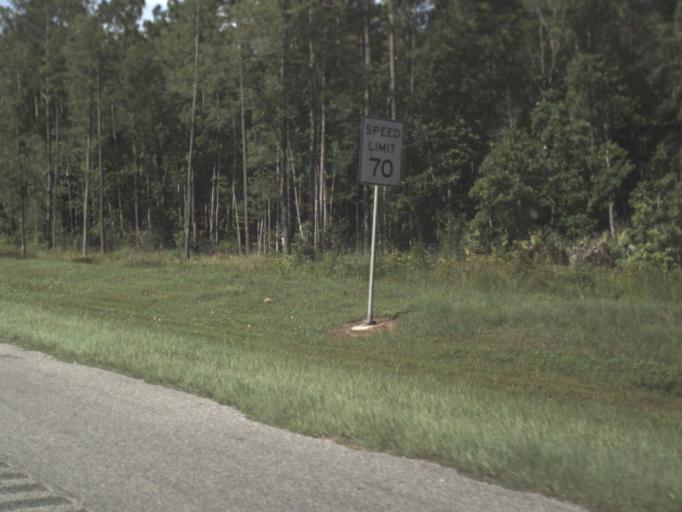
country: US
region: Florida
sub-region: Saint Johns County
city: Fruit Cove
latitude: 30.0526
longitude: -81.4975
